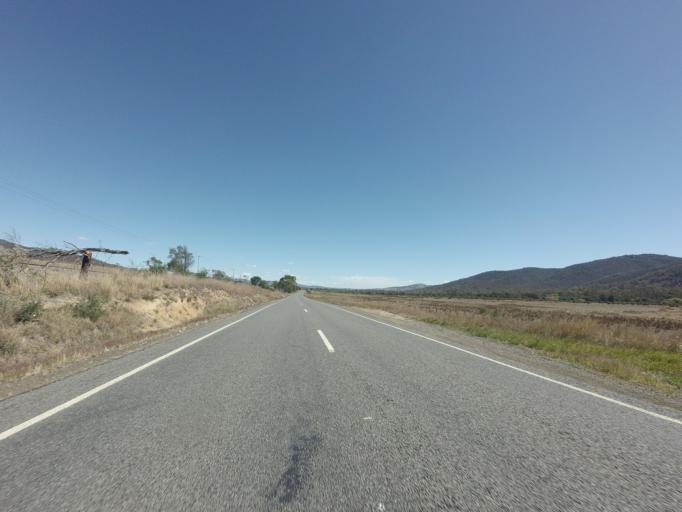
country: AU
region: Tasmania
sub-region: Northern Midlands
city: Evandale
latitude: -41.7420
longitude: 147.7913
